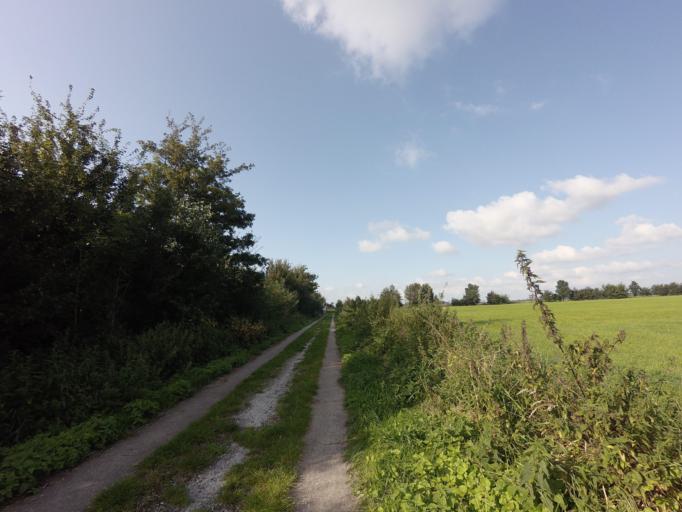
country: NL
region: Flevoland
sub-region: Gemeente Noordoostpolder
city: Ens
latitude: 52.6568
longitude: 5.7748
